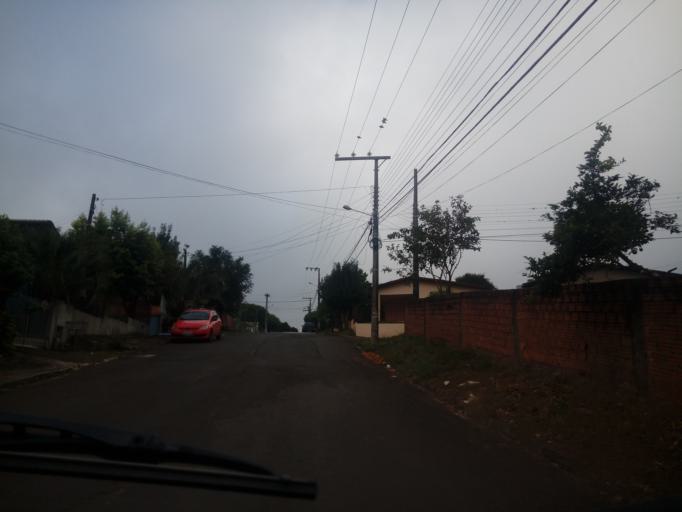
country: BR
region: Santa Catarina
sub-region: Chapeco
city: Chapeco
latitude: -27.1145
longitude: -52.6244
